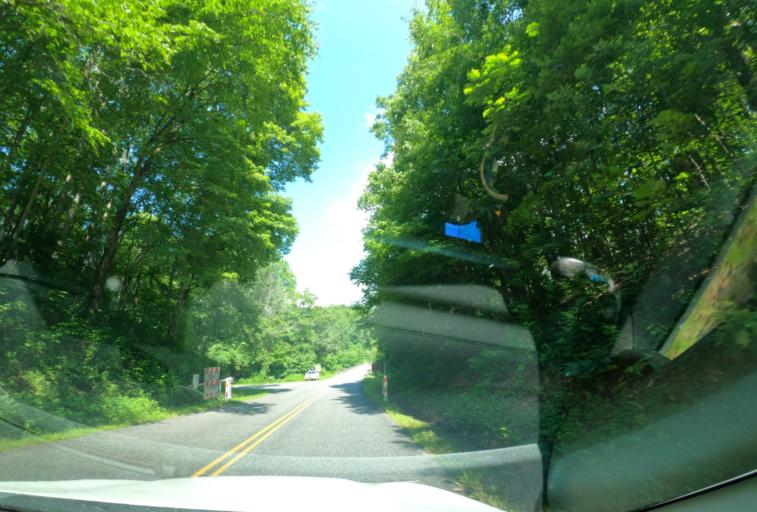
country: US
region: North Carolina
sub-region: Haywood County
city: Hazelwood
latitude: 35.4336
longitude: -83.0765
